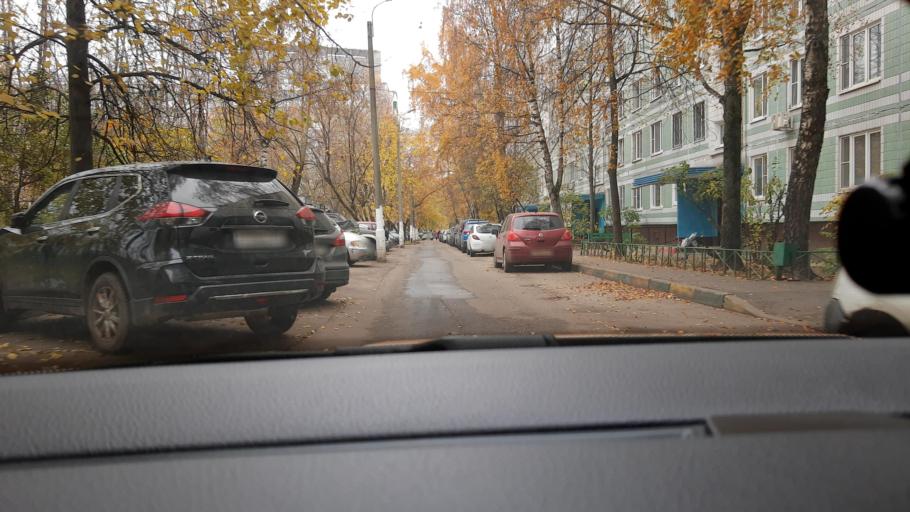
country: RU
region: Moscow
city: Otradnoye
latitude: 55.8685
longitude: 37.6015
